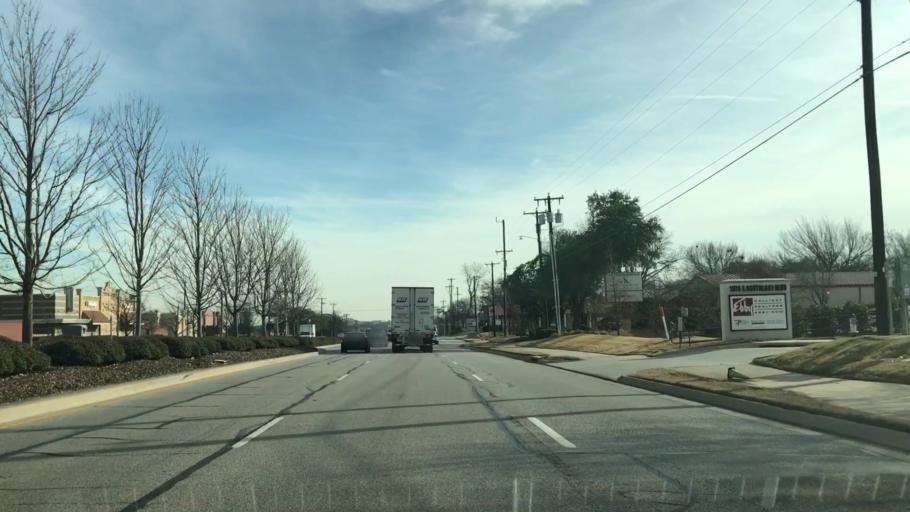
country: US
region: Texas
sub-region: Tarrant County
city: Southlake
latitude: 32.9409
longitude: -97.1275
